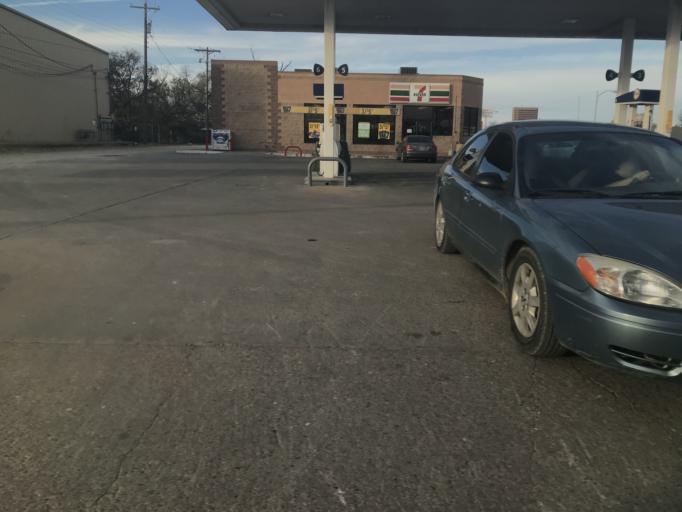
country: US
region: Texas
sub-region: Taylor County
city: Abilene
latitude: 32.4322
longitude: -99.7390
